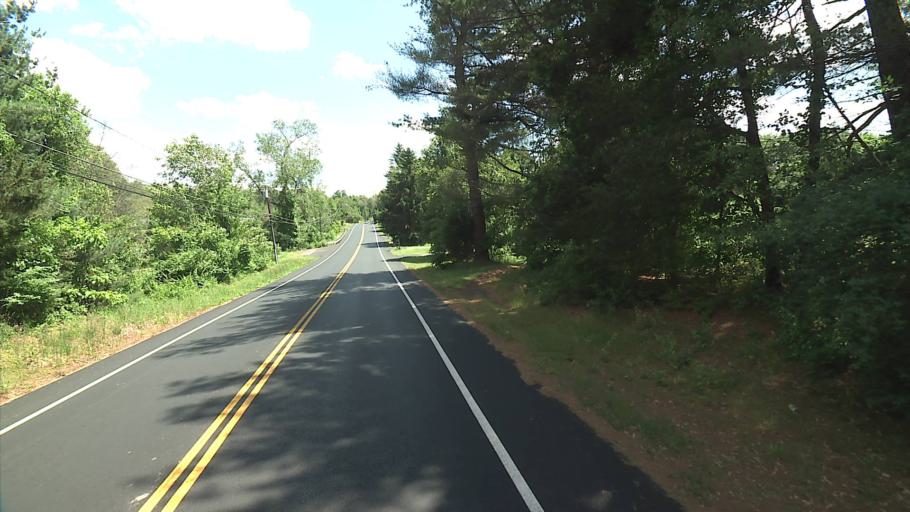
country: US
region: Connecticut
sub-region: Tolland County
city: Somers
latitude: 42.0039
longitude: -72.4364
